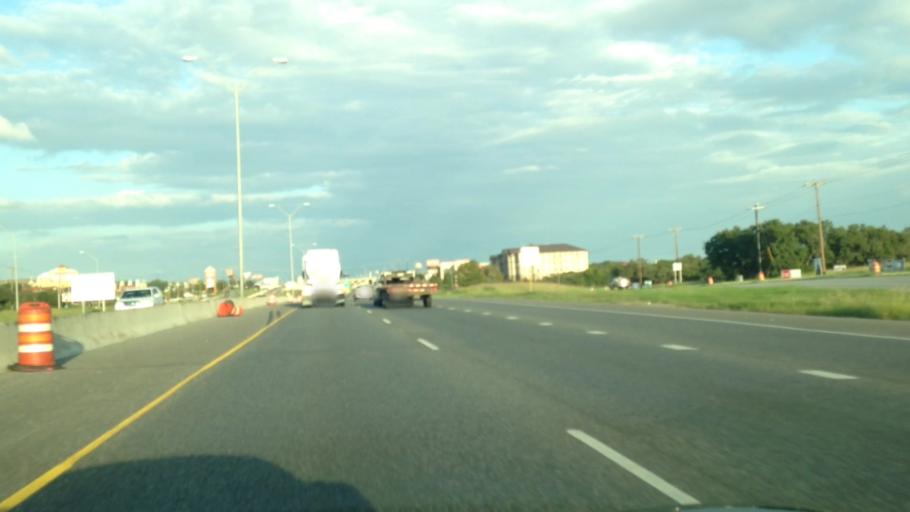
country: US
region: Texas
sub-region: Bexar County
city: Hollywood Park
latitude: 29.6089
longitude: -98.4844
